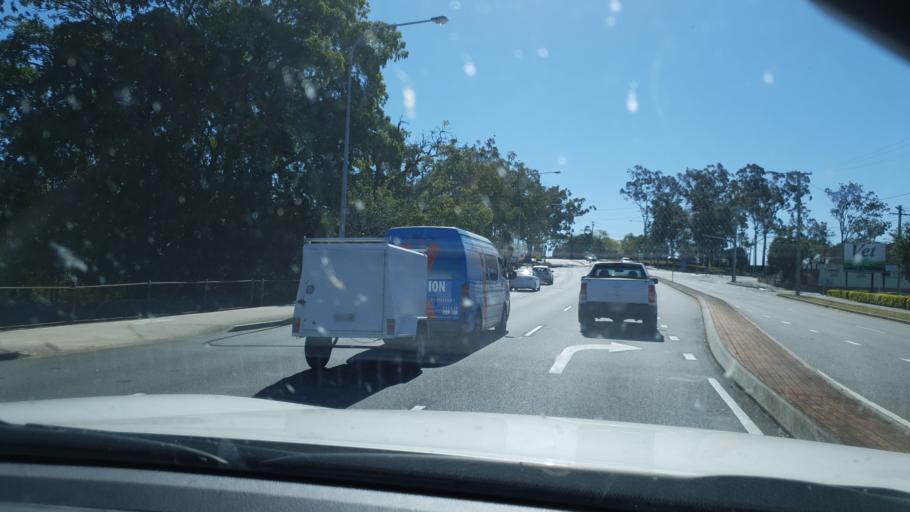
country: AU
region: Queensland
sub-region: Brisbane
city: Woolloongabba
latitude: -27.4987
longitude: 153.0278
